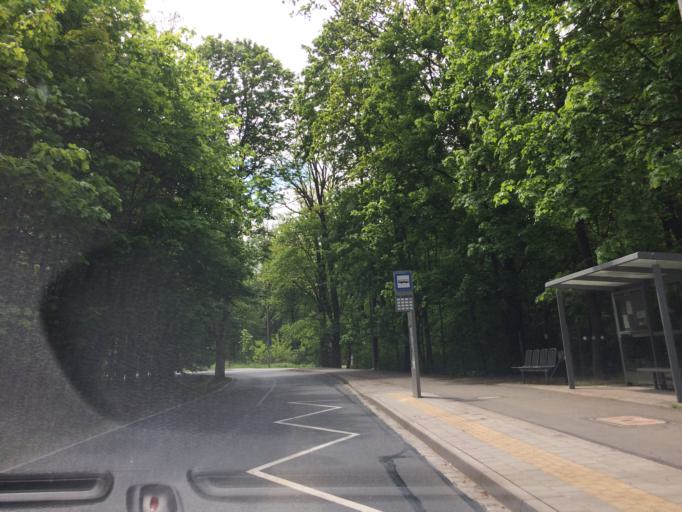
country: PL
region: Lower Silesian Voivodeship
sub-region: Powiat wroclawski
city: Smolec
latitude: 51.1553
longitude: 16.8732
